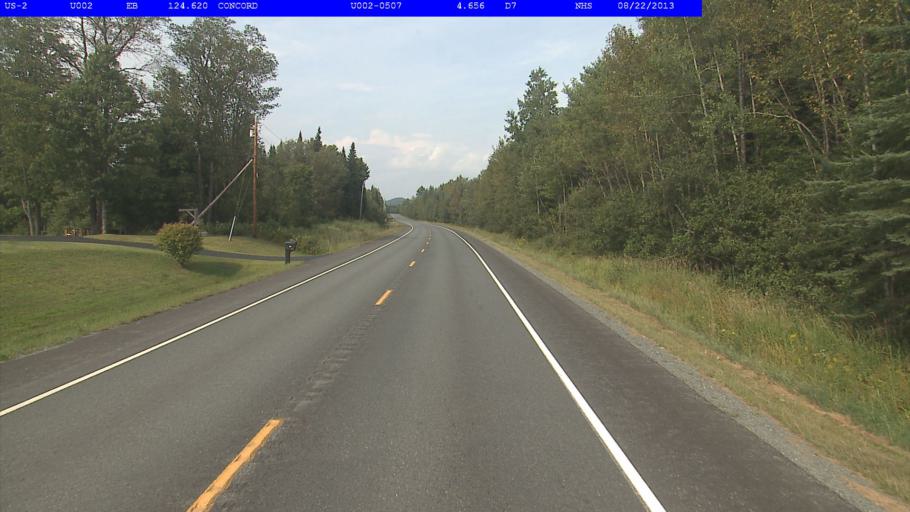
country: US
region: Vermont
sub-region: Caledonia County
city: St Johnsbury
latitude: 44.4588
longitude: -71.8648
